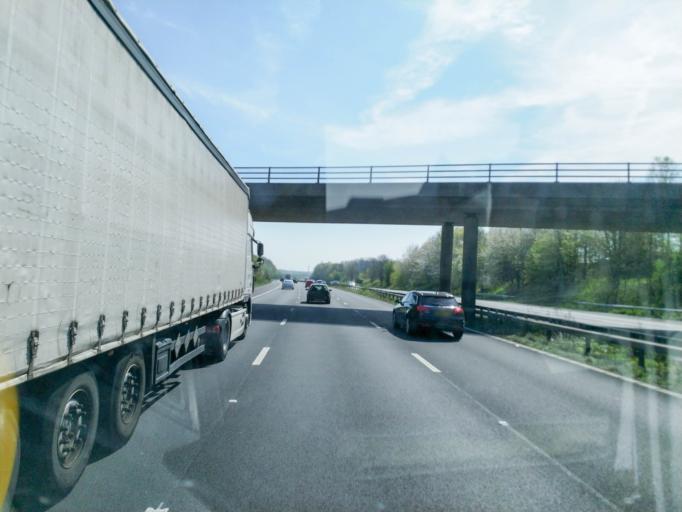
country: GB
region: England
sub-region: Kent
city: Wye
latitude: 51.1150
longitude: 0.9545
